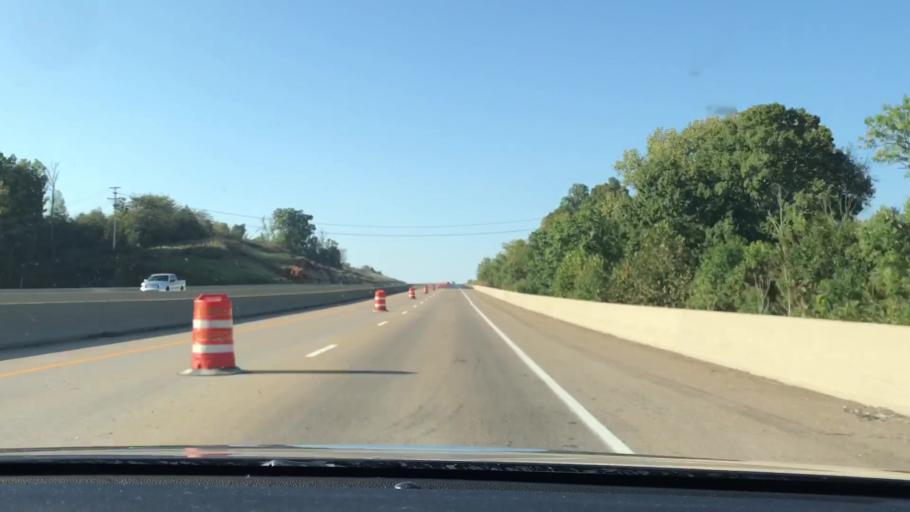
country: US
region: Kentucky
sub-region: Trigg County
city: Cadiz
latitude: 36.8535
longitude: -87.8167
